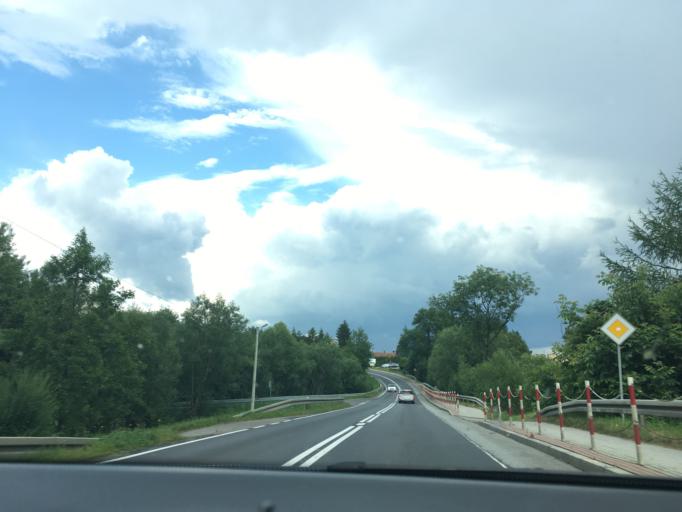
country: PL
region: Subcarpathian Voivodeship
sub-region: Powiat krosnienski
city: Kroscienko Wyzne
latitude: 49.6566
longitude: 21.8311
